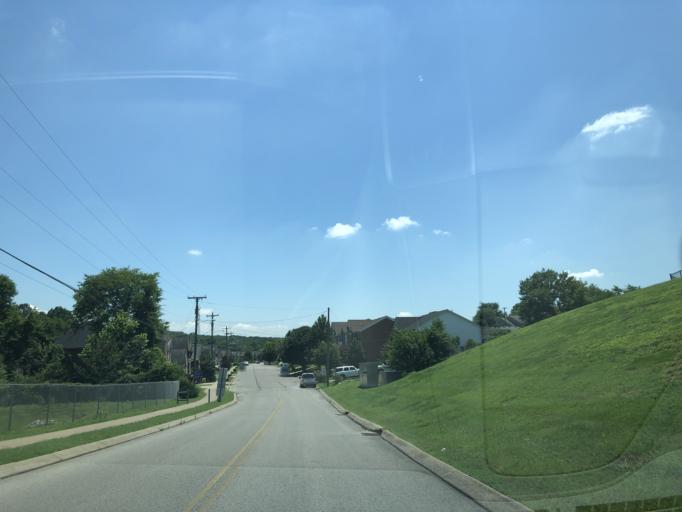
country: US
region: Tennessee
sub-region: Williamson County
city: Nolensville
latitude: 36.0225
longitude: -86.6586
